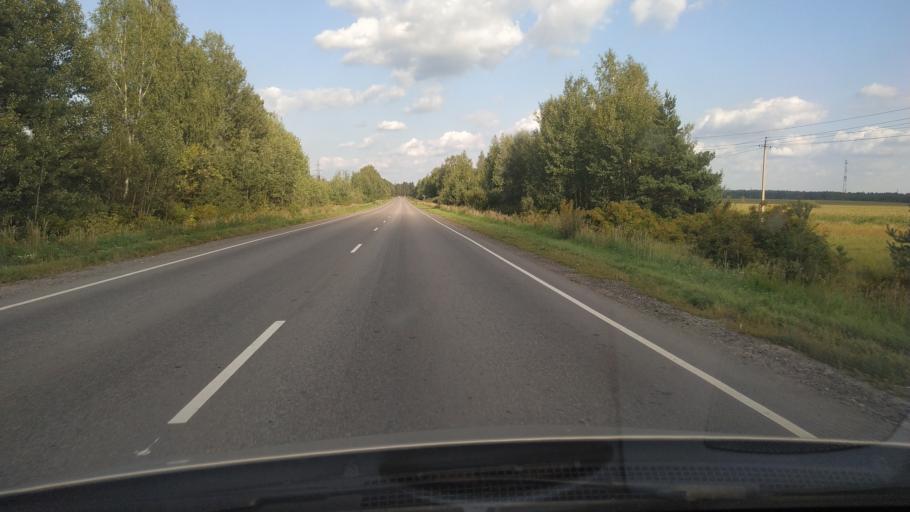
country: RU
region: Moskovskaya
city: Vereya
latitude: 55.7076
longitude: 39.1323
